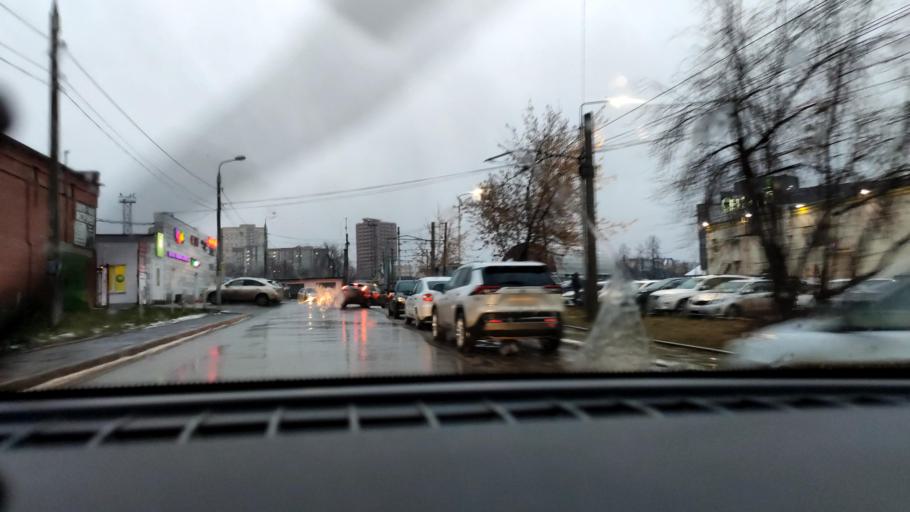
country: RU
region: Perm
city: Perm
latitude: 57.9781
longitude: 56.1904
